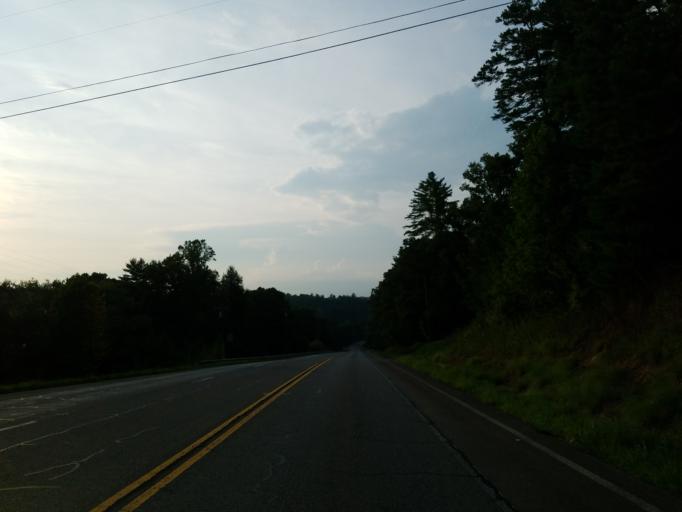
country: US
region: Georgia
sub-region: Gilmer County
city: Ellijay
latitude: 34.6687
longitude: -84.4541
